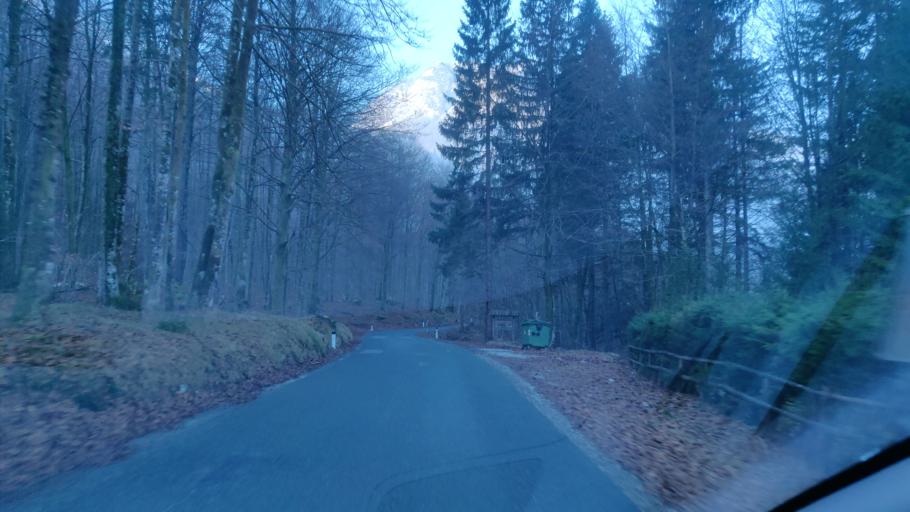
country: SI
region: Bohinj
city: Bohinjska Bistrica
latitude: 46.2762
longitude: 13.8295
